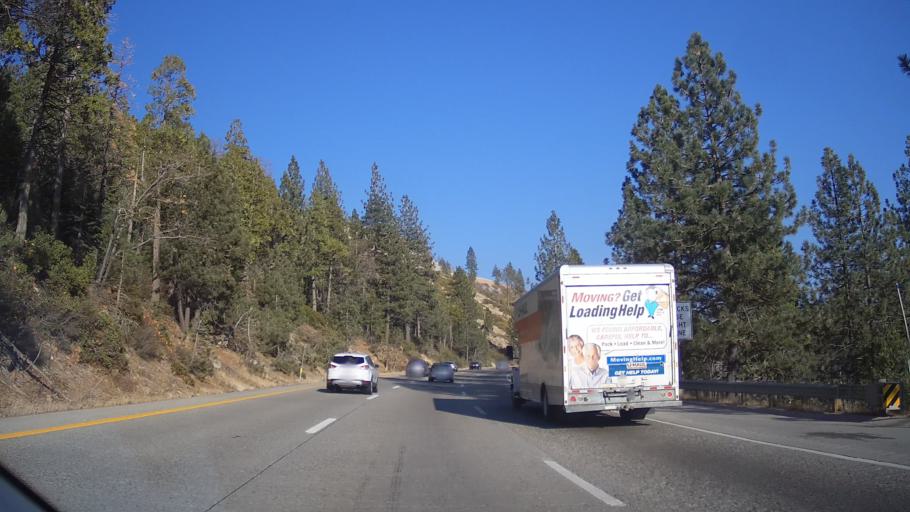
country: US
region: California
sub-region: Sierra County
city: Downieville
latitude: 39.3089
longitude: -120.6400
